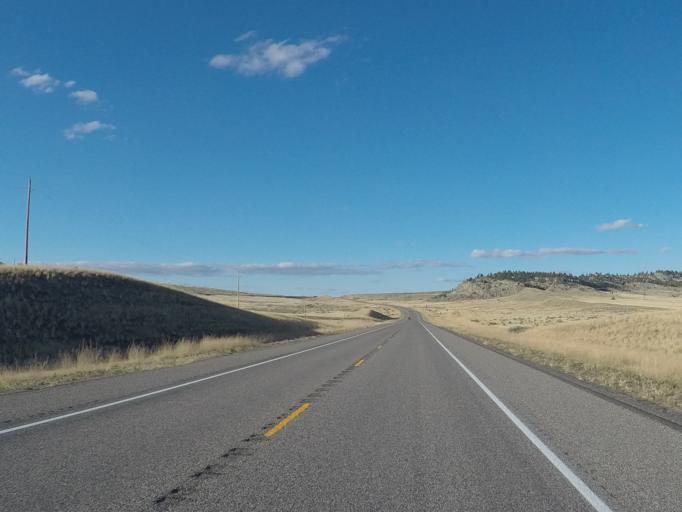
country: US
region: Montana
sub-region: Yellowstone County
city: Billings
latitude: 45.9017
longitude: -108.6677
